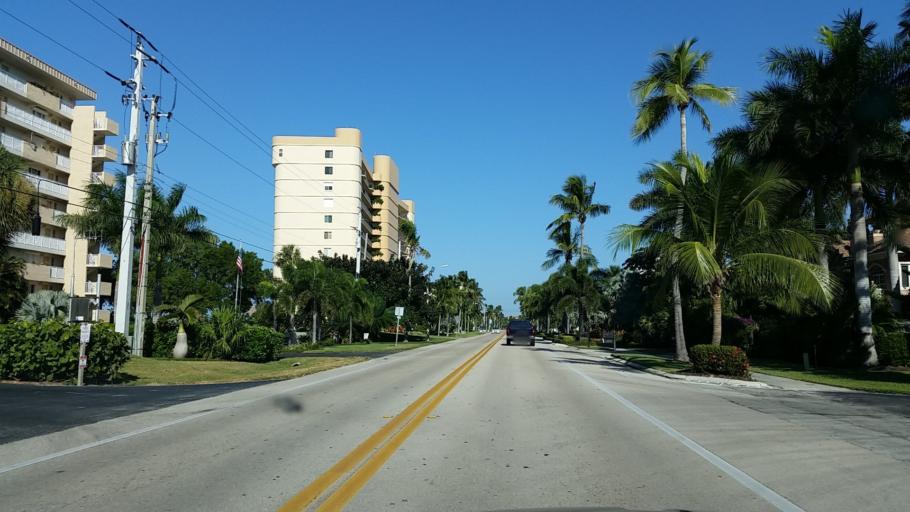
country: US
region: Florida
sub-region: Lee County
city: Bonita Springs
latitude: 26.3543
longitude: -81.8560
